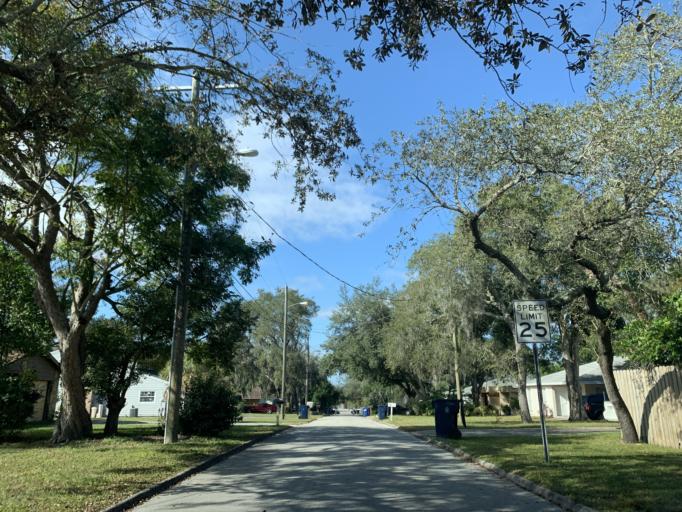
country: US
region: Florida
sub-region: Hillsborough County
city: Temple Terrace
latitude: 28.0384
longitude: -82.4101
